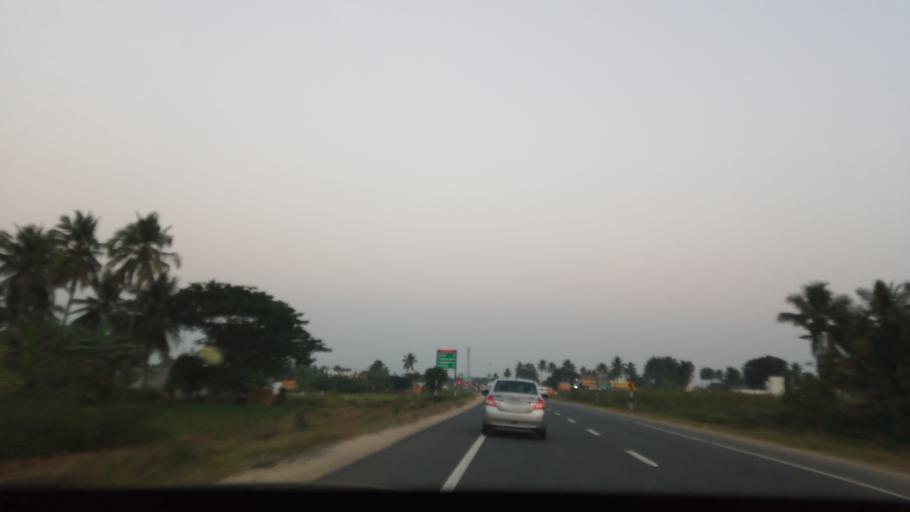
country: IN
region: Tamil Nadu
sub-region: Salem
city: Belur
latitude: 11.6496
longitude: 78.3957
